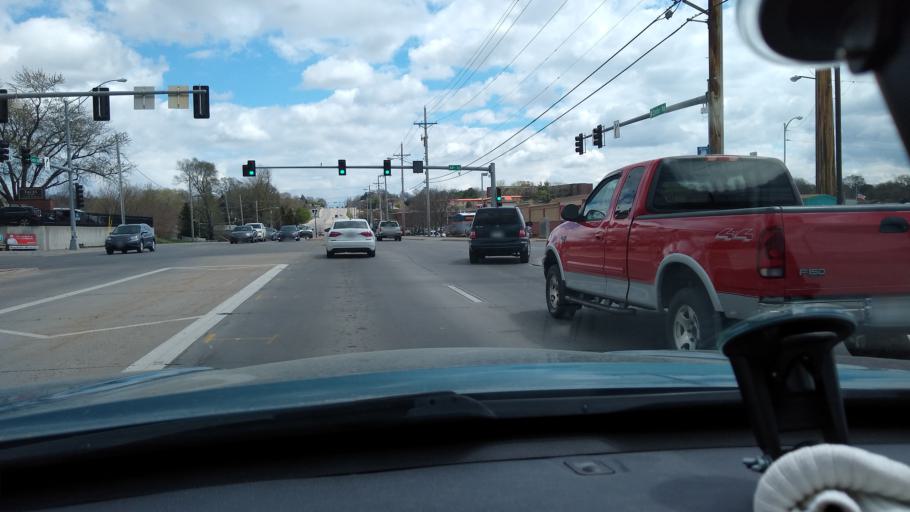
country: US
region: Nebraska
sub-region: Douglas County
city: Ralston
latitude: 41.2342
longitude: -96.0436
